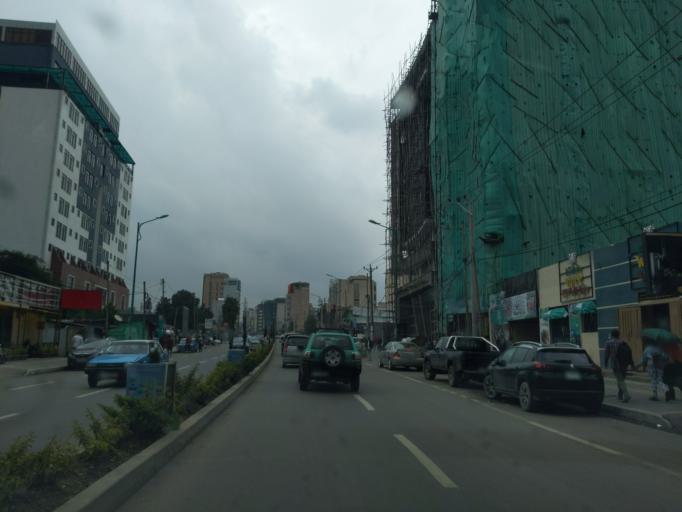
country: ET
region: Adis Abeba
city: Addis Ababa
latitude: 8.9899
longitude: 38.7657
